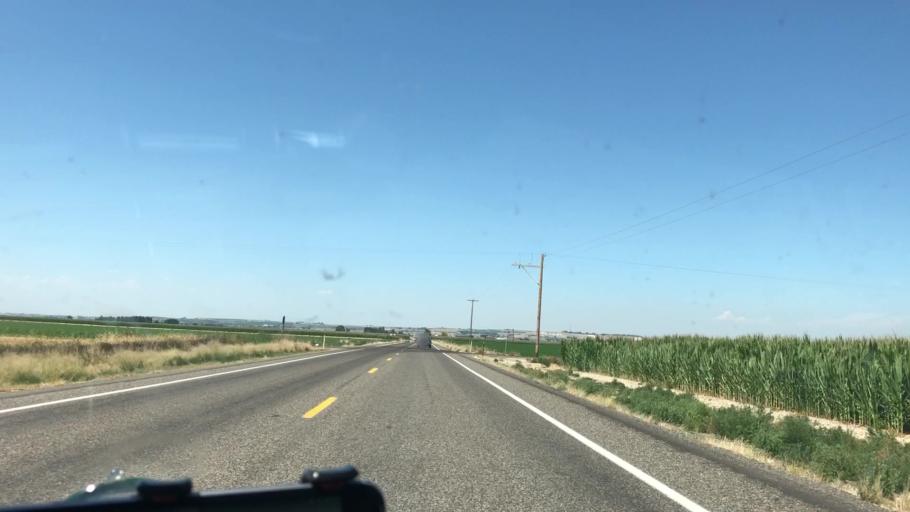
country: US
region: Idaho
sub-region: Owyhee County
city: Marsing
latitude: 43.5301
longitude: -116.8515
